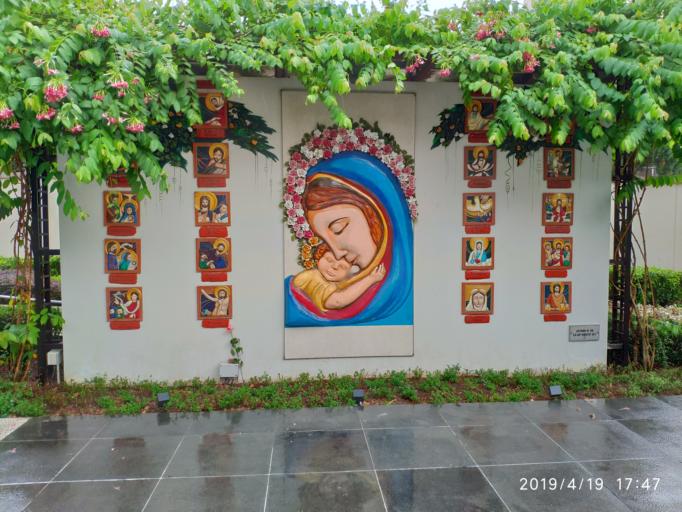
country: MY
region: Johor
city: Johor Bahru
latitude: 1.3683
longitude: 103.7670
